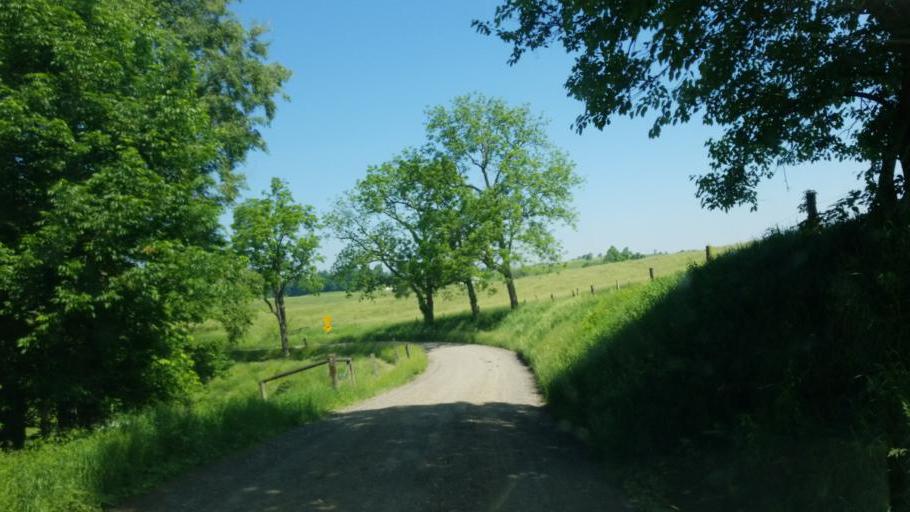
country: US
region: Ohio
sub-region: Holmes County
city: Millersburg
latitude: 40.4807
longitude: -81.7942
